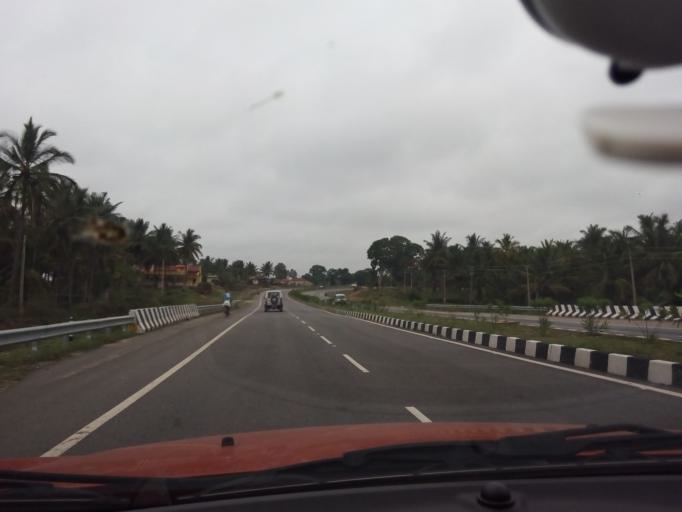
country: IN
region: Karnataka
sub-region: Hassan
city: Shravanabelagola
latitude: 12.9441
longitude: 76.5500
